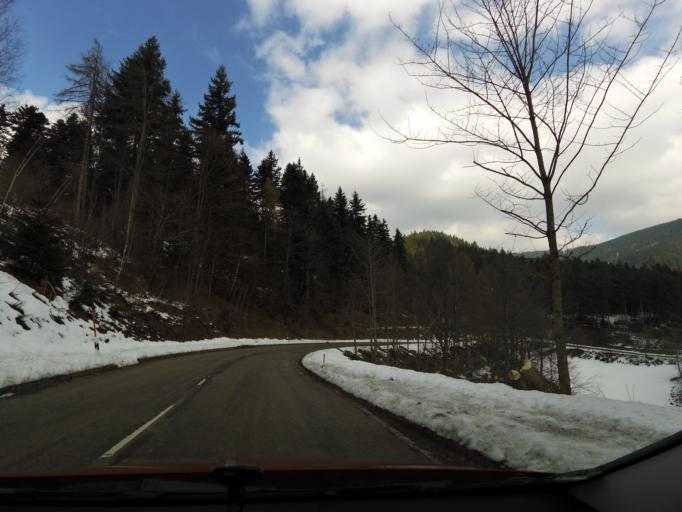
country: DE
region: Baden-Wuerttemberg
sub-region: Freiburg Region
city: Seebach
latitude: 48.5374
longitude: 8.1918
